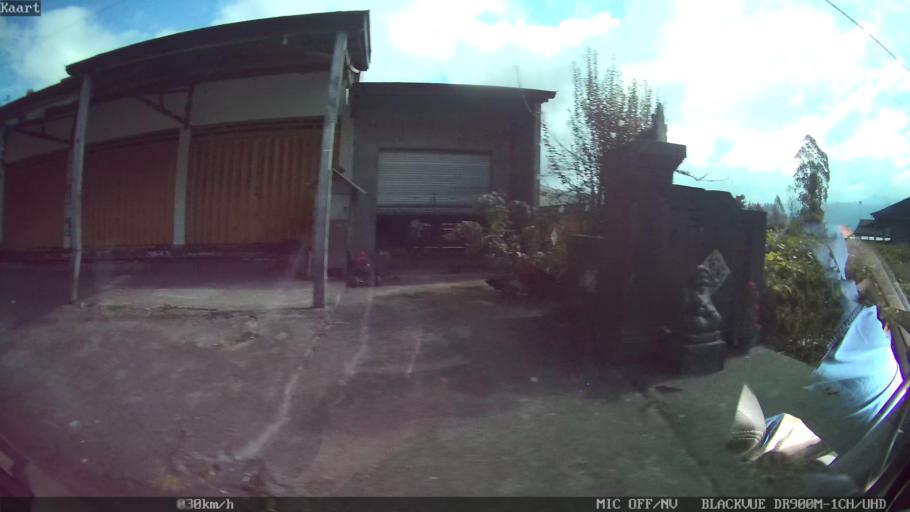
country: ID
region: Bali
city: Banjar Trunyan
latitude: -8.2182
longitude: 115.3921
